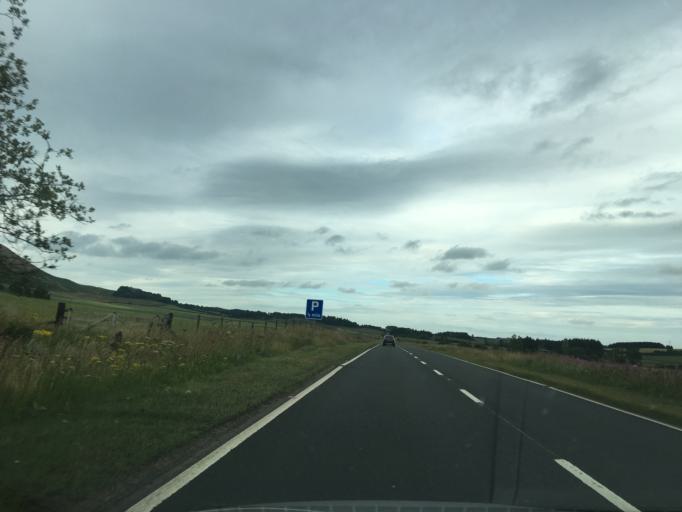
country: GB
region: Scotland
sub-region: The Scottish Borders
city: West Linton
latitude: 55.7189
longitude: -3.4075
